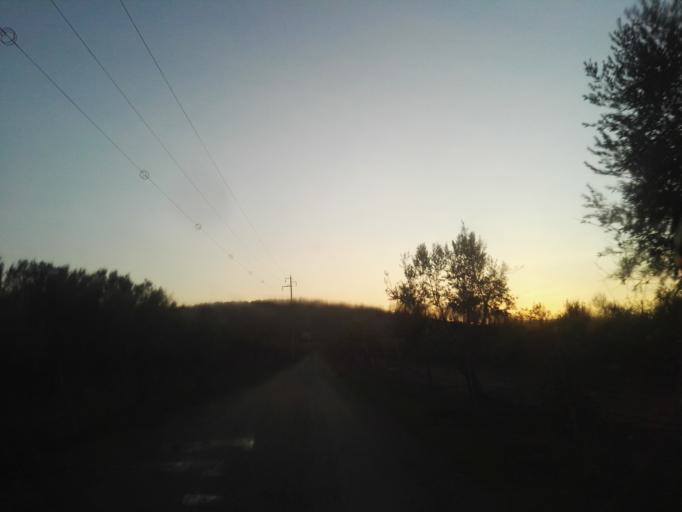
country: PT
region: Evora
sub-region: Montemor-O-Novo
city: Montemor-o-Novo
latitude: 38.6424
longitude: -8.1304
